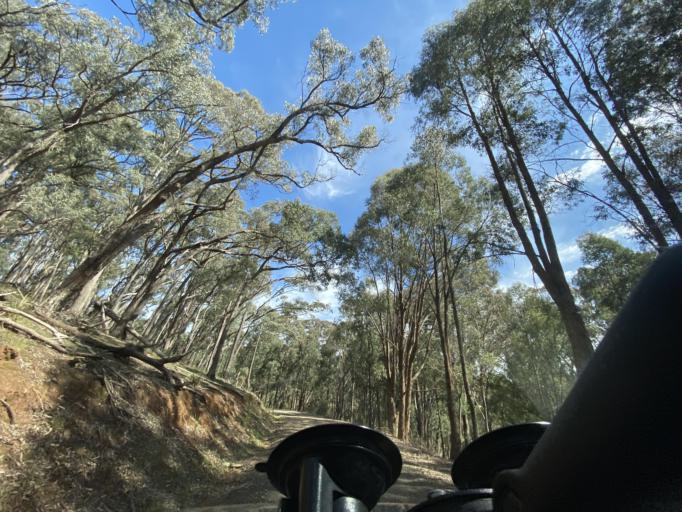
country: AU
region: Victoria
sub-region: Mansfield
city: Mansfield
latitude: -36.8138
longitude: 146.1026
